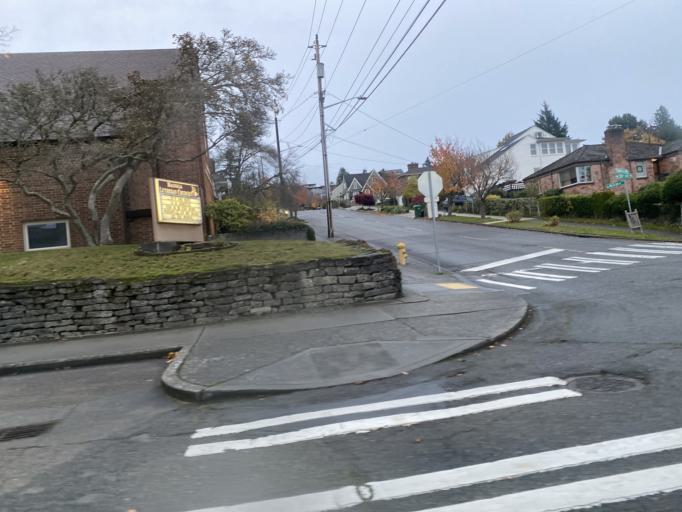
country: US
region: Washington
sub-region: King County
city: Seattle
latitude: 47.6397
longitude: -122.3970
